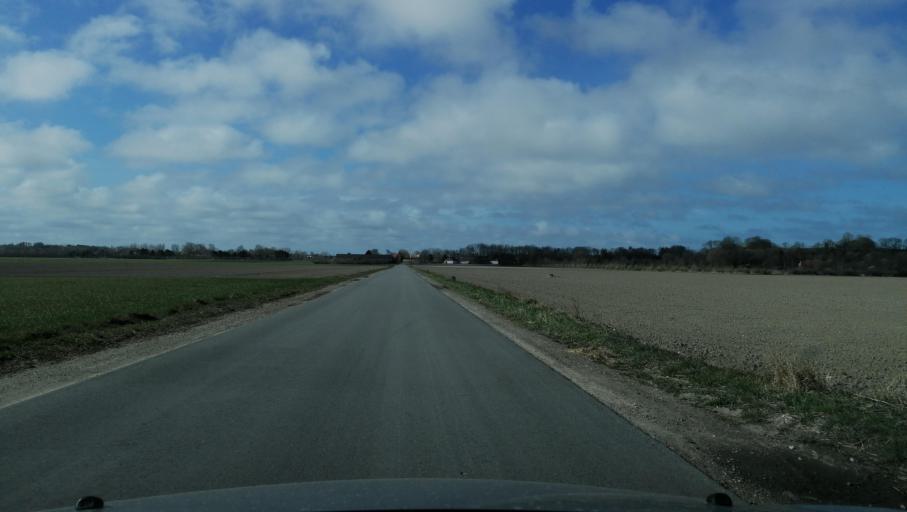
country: DK
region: Zealand
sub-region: Odsherred Kommune
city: Horve
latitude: 55.7790
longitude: 11.4319
